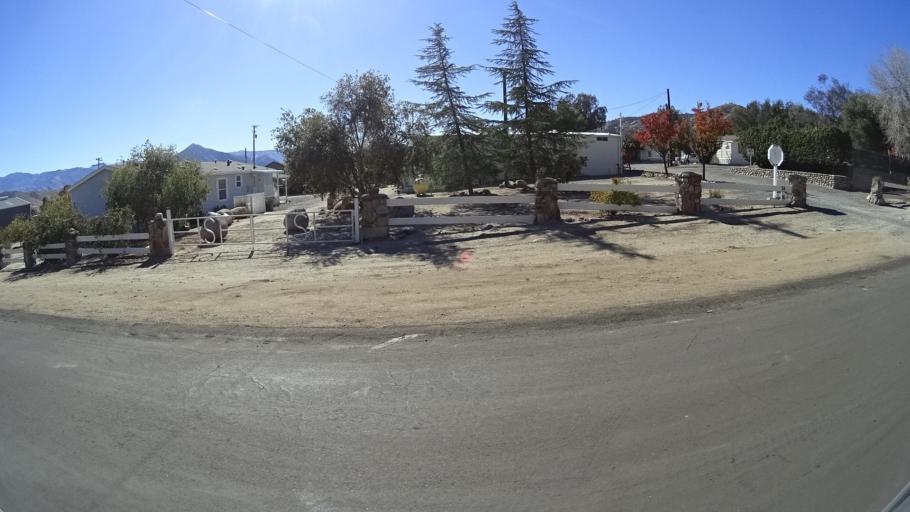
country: US
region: California
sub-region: Kern County
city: Wofford Heights
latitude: 35.7066
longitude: -118.4550
